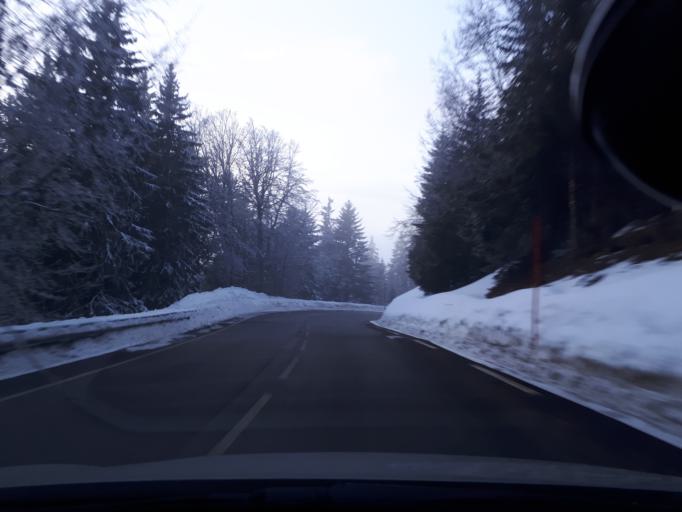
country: FR
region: Rhone-Alpes
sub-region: Departement de l'Isere
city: Vaulnaveys-le-Bas
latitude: 45.0976
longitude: 5.8652
